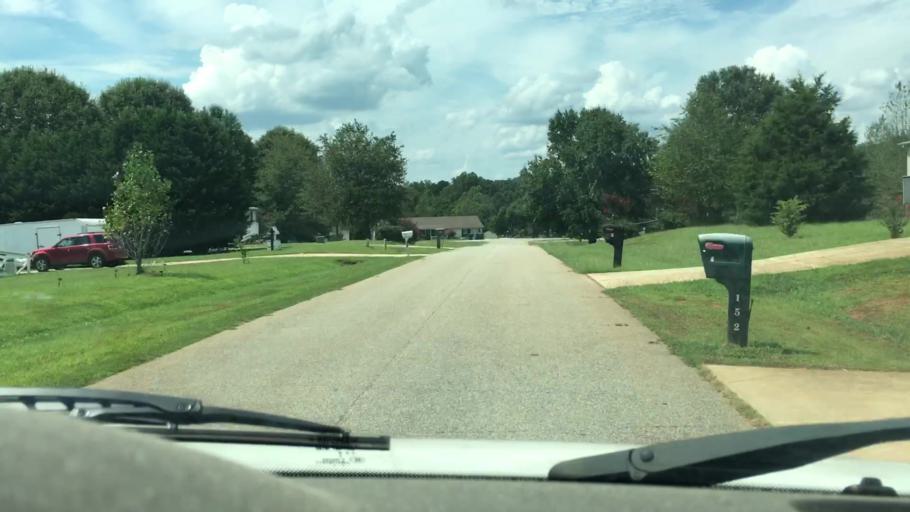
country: US
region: North Carolina
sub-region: Iredell County
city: Mooresville
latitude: 35.6748
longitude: -80.7866
